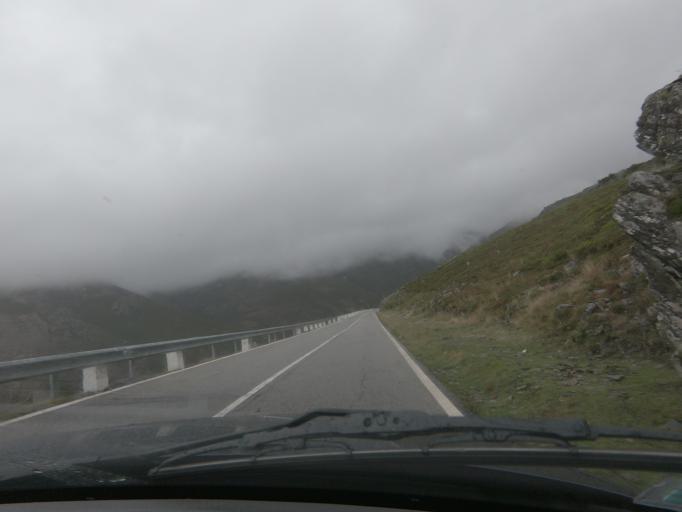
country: PT
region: Vila Real
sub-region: Mondim de Basto
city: Mondim de Basto
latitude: 41.3391
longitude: -7.8773
